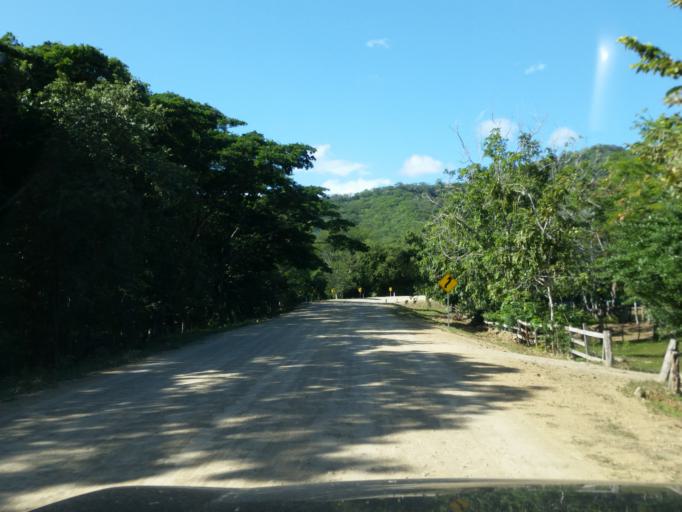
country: NI
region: Rivas
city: San Juan del Sur
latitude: 11.1735
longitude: -85.8001
